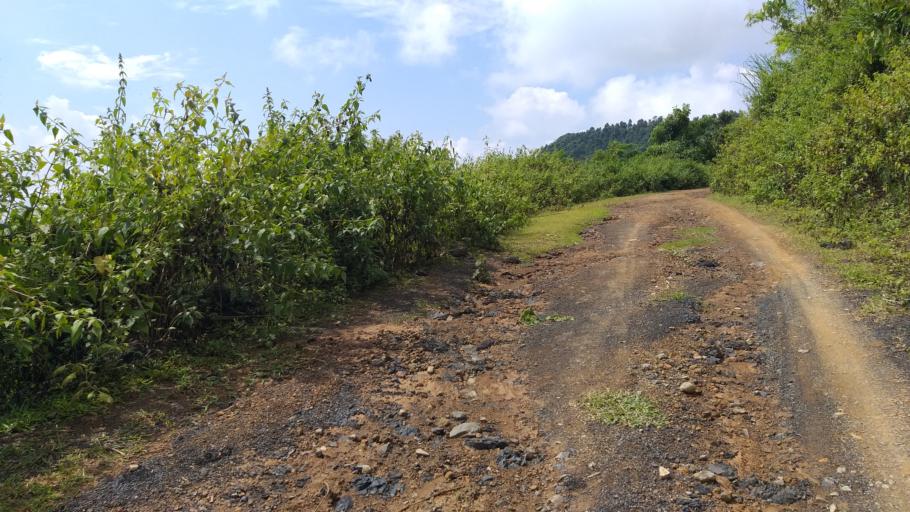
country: VN
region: Huyen Dien Bien
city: Dien Bien Phu
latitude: 21.4169
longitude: 102.6845
